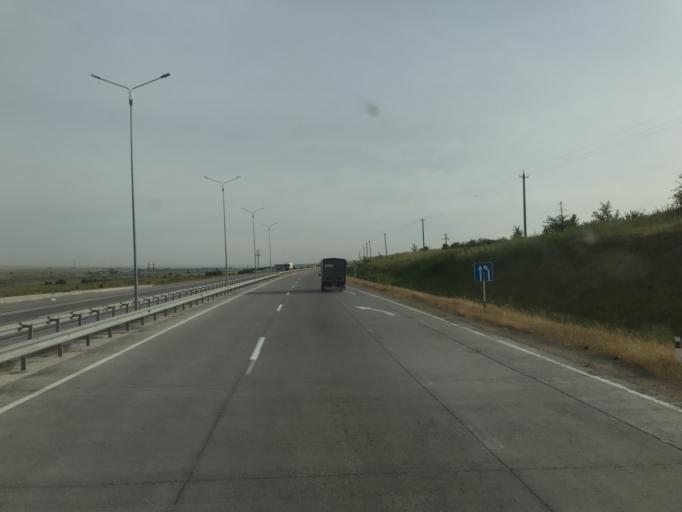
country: KZ
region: Ongtustik Qazaqstan
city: Qazyqurt
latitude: 41.6919
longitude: 69.3947
